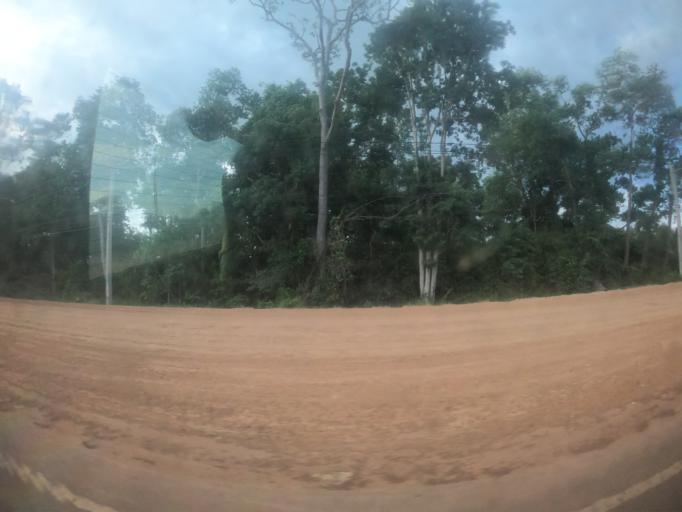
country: TH
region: Surin
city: Kap Choeng
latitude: 14.4623
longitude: 103.6523
